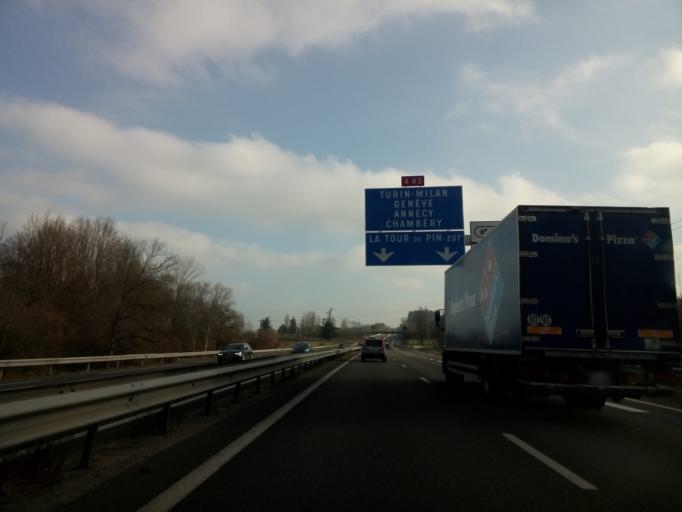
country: FR
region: Rhone-Alpes
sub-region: Departement de l'Isere
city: Saint-Jean-de-Soudain
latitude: 45.5607
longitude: 5.4209
